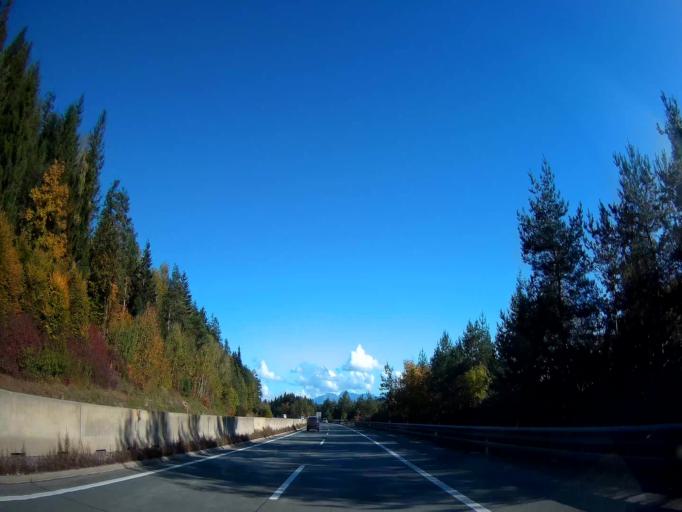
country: AT
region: Carinthia
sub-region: Politischer Bezirk Klagenfurt Land
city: Maria Worth
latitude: 46.6284
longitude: 14.1855
